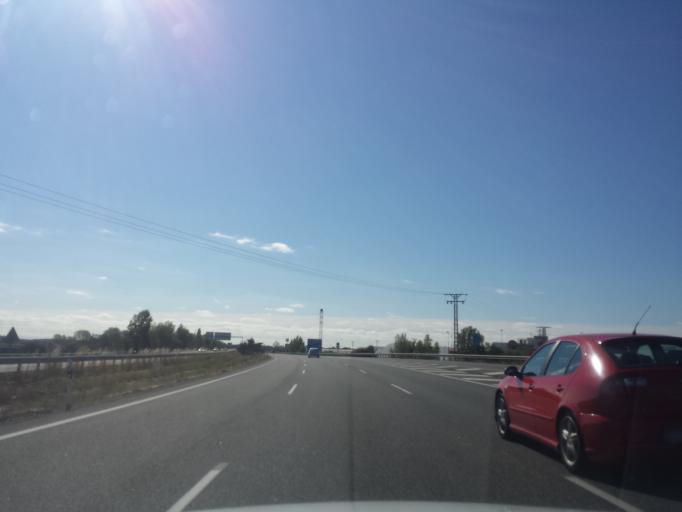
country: ES
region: Castille and Leon
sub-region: Provincia de Zamora
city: Villanueva de Azoague
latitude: 41.9979
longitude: -5.6541
